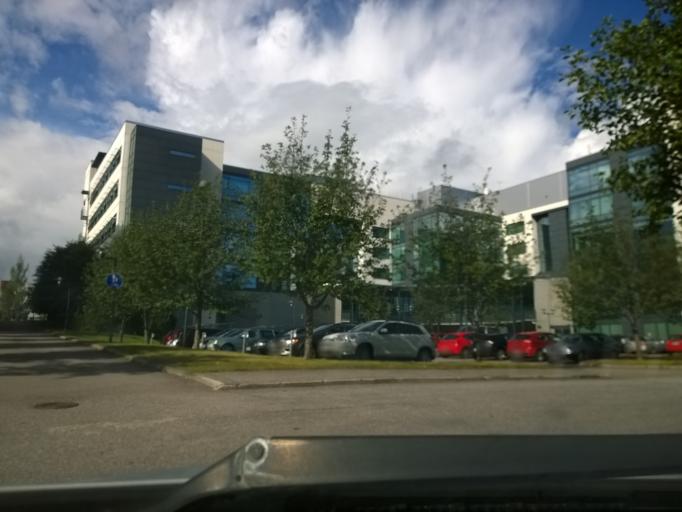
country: FI
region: Pirkanmaa
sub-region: Tampere
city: Tampere
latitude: 61.4479
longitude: 23.8651
